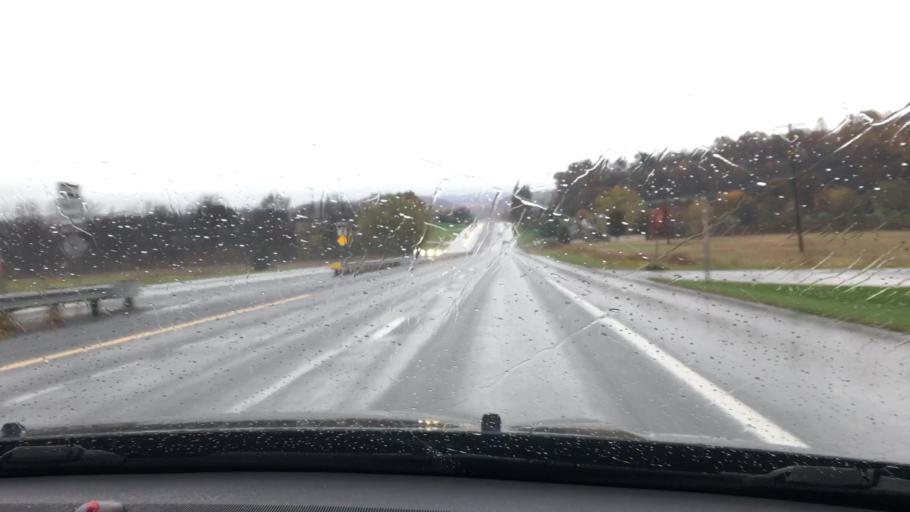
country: US
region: Pennsylvania
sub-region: Lancaster County
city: Willow Street
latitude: 39.9546
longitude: -76.2649
